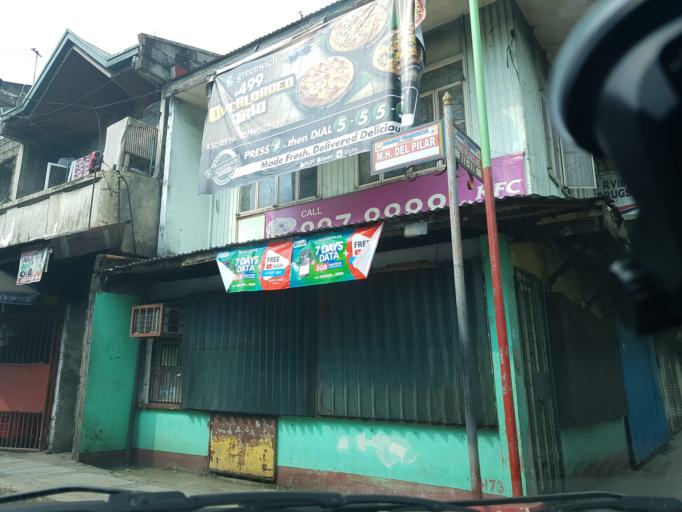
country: PH
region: Calabarzon
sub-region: Province of Rizal
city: Pateros
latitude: 14.5554
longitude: 121.0924
